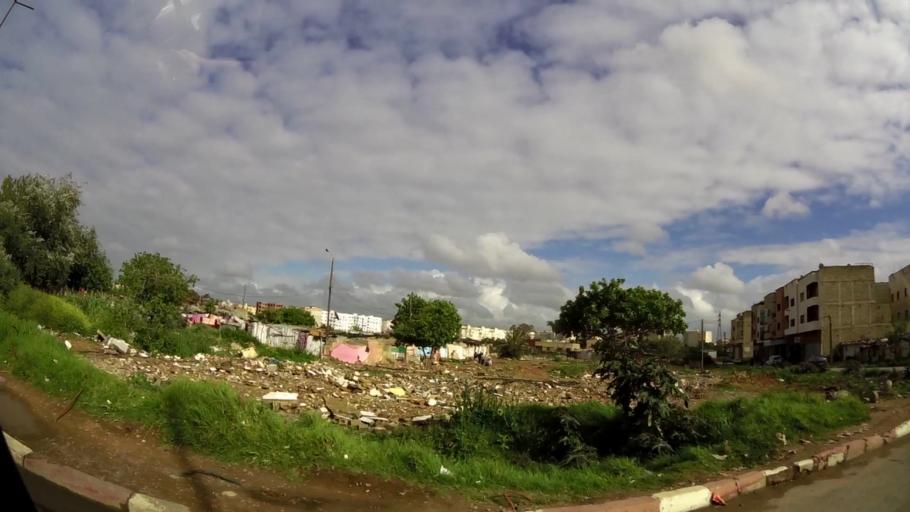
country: MA
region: Grand Casablanca
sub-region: Mohammedia
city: Mohammedia
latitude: 33.6941
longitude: -7.3699
